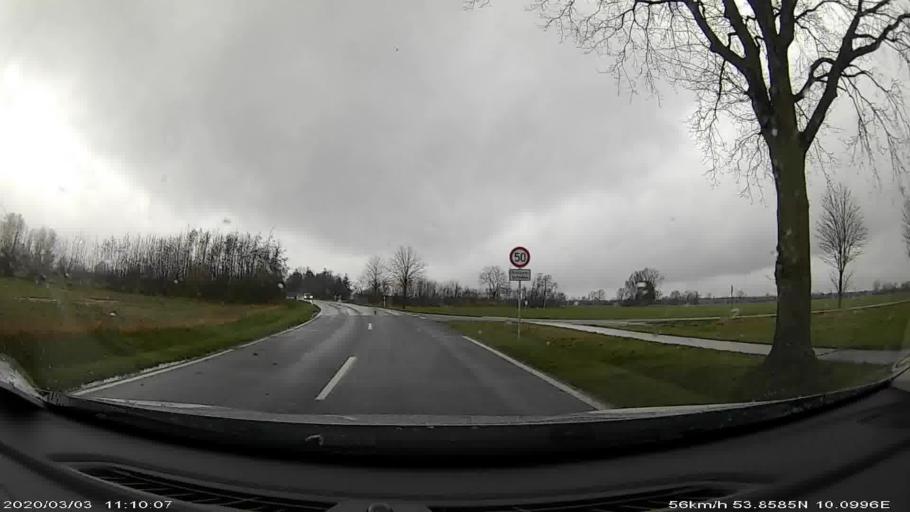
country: DE
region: Schleswig-Holstein
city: Sievershutten
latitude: 53.8599
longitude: 10.0952
